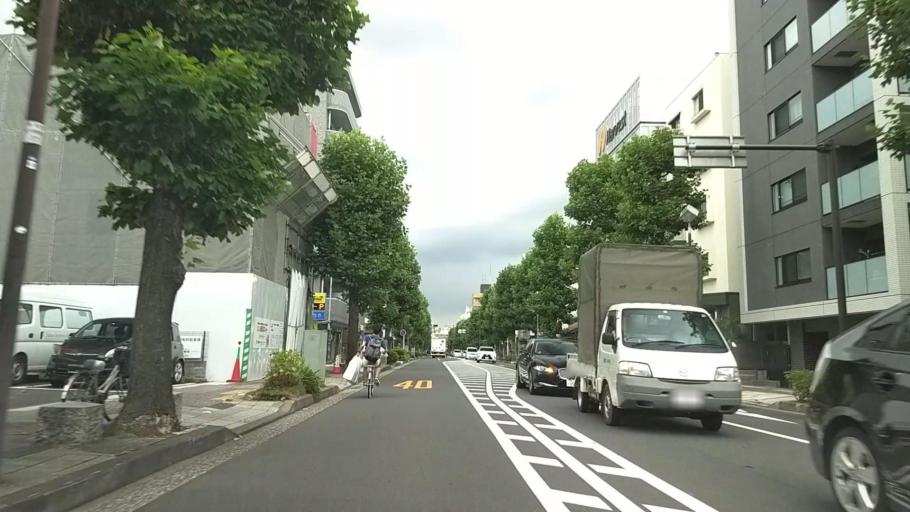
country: JP
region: Kanagawa
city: Yokohama
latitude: 35.4492
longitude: 139.5996
